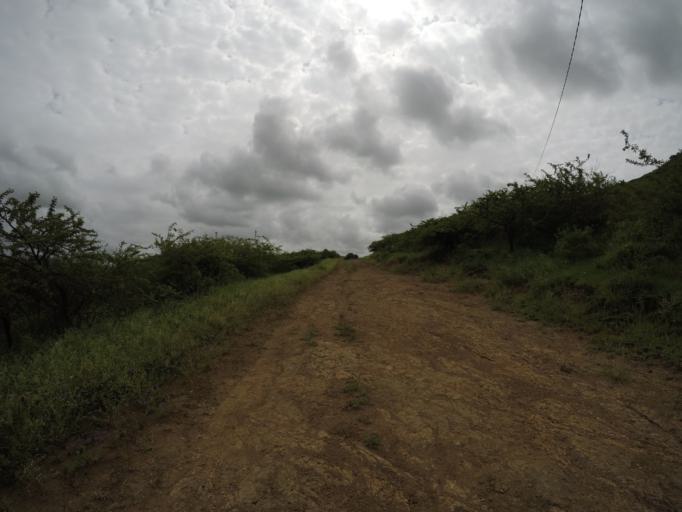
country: ZA
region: KwaZulu-Natal
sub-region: uThungulu District Municipality
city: Empangeni
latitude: -28.6168
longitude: 31.8872
